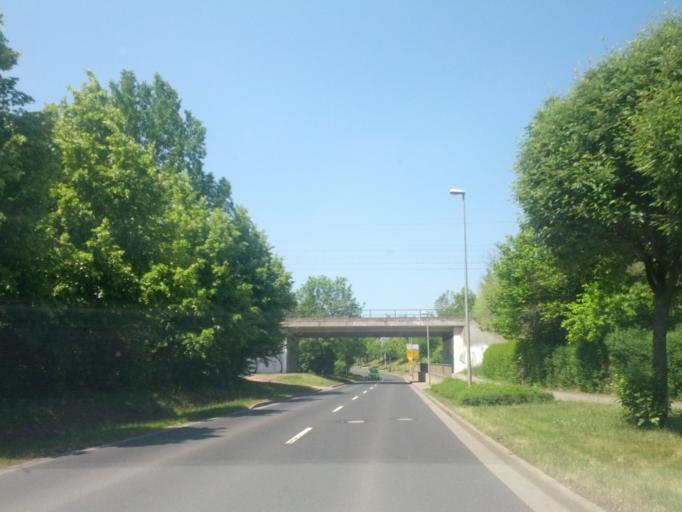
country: DE
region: Thuringia
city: Gotha
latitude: 50.9326
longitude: 10.6806
